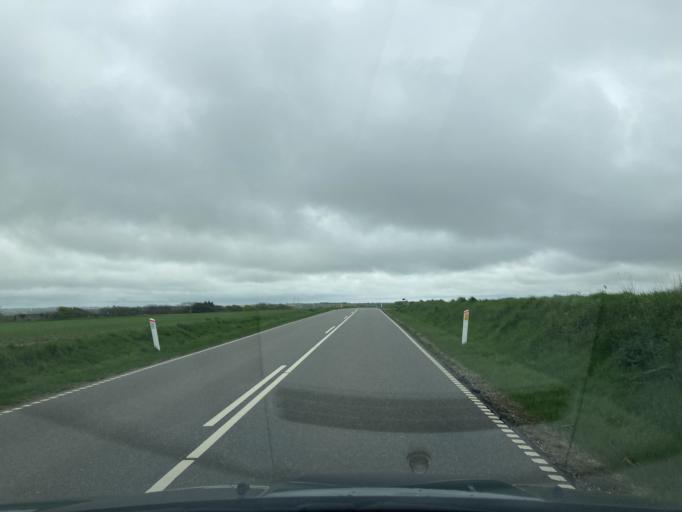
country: DK
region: North Denmark
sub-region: Thisted Kommune
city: Hurup
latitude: 56.8224
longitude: 8.3528
